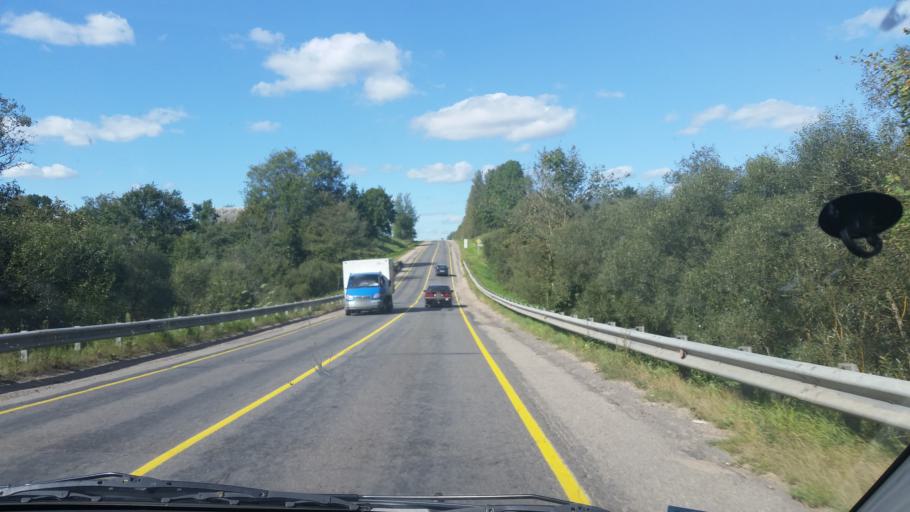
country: BY
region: Vitebsk
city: Vitebsk
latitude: 55.1184
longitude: 30.2798
